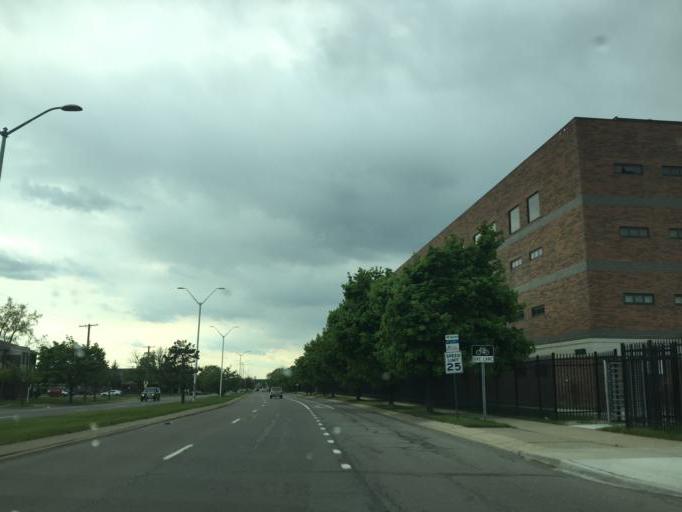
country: US
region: Michigan
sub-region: Wayne County
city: Detroit
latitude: 42.3379
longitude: -83.0855
